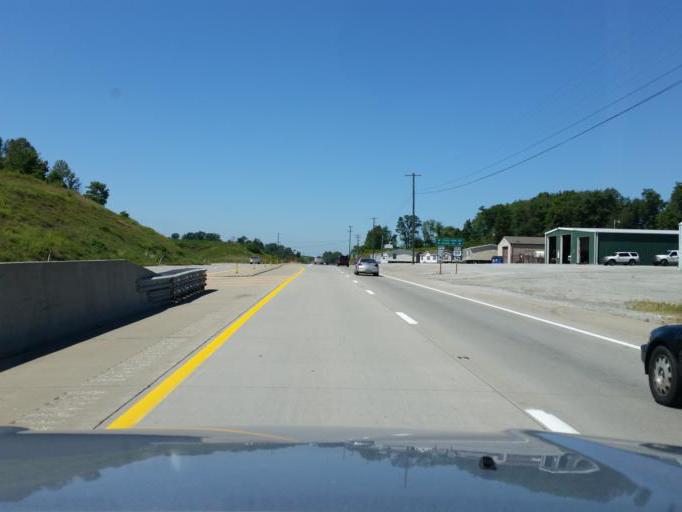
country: US
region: Pennsylvania
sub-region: Westmoreland County
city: Loyalhanna
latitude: 40.4186
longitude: -79.3672
